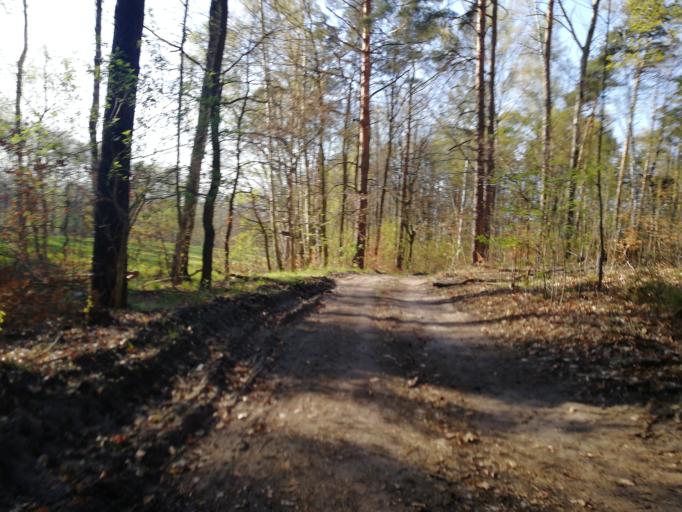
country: DE
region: Brandenburg
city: Calau
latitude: 51.7194
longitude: 13.9592
